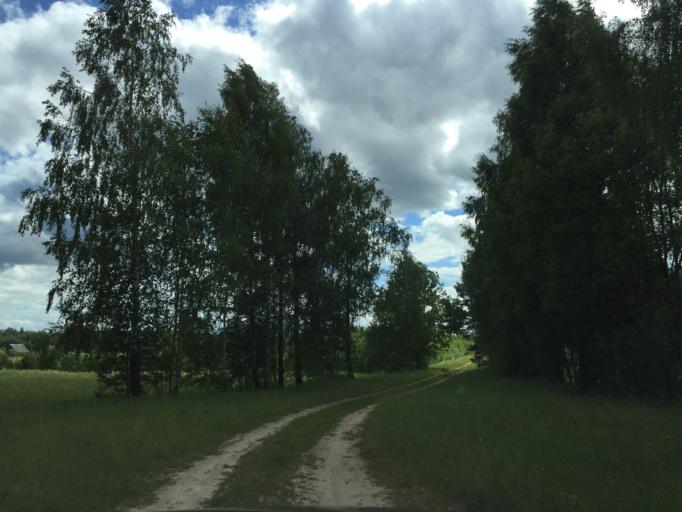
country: LV
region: Lecava
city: Iecava
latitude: 56.5590
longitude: 24.3443
